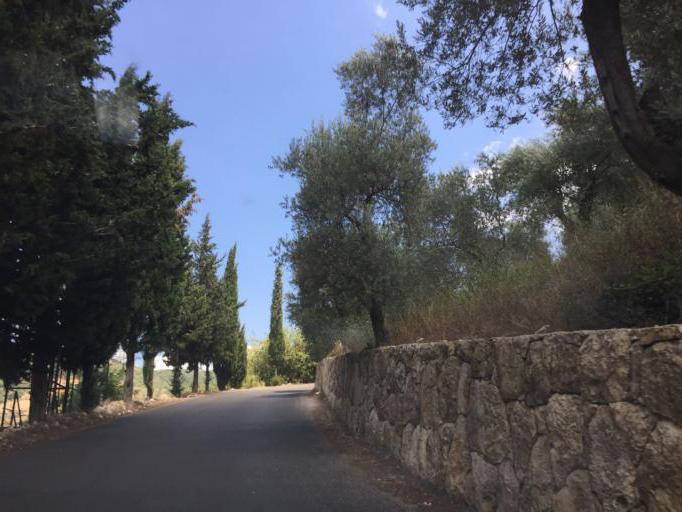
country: LB
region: Mont-Liban
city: Beit ed Dine
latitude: 33.6960
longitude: 35.5783
